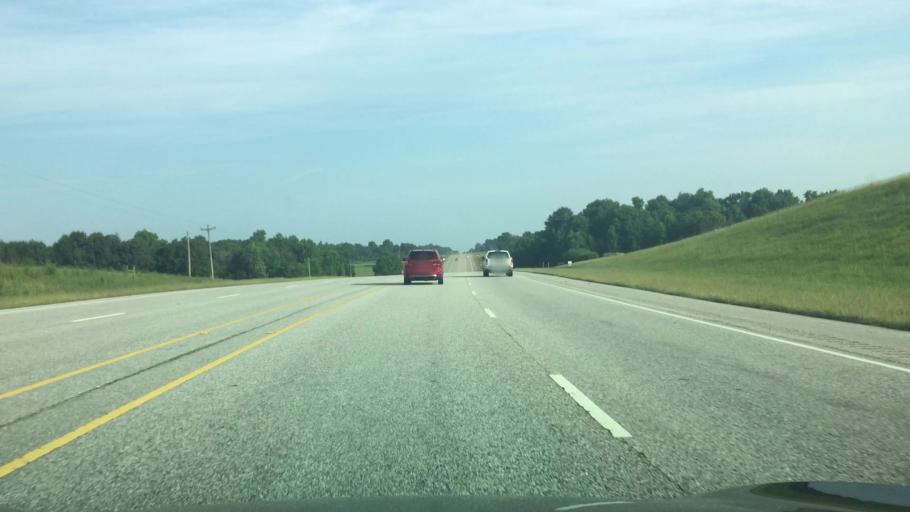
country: US
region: Alabama
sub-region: Butler County
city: Georgiana
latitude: 31.5208
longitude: -86.7137
